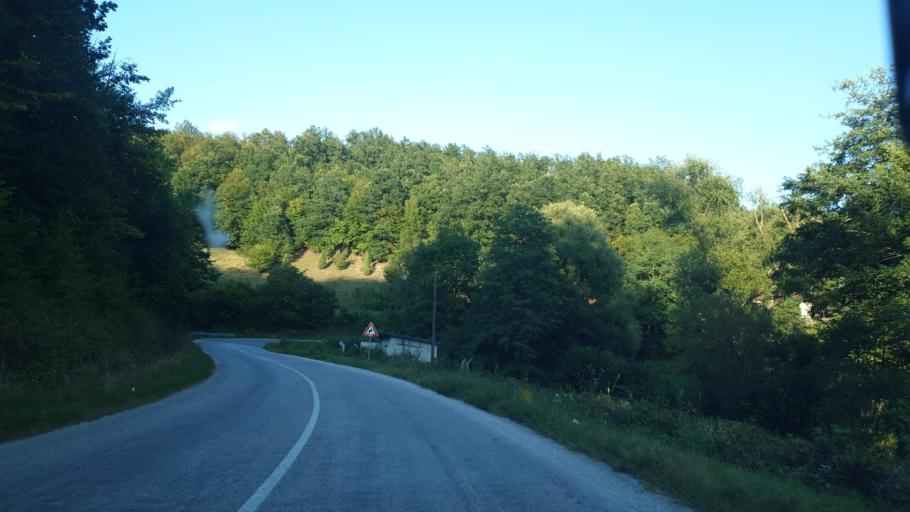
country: RS
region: Central Serbia
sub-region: Zlatiborski Okrug
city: Pozega
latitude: 43.9500
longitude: 20.0231
